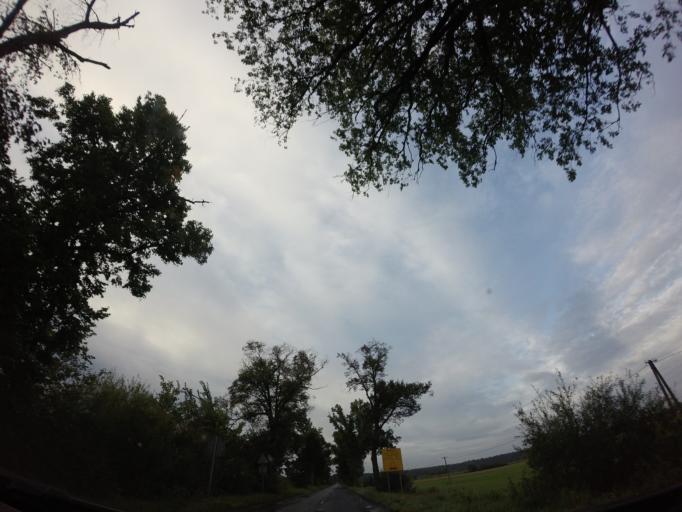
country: PL
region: Lubusz
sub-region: Powiat strzelecko-drezdenecki
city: Drezdenko
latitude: 52.8227
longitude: 15.8279
